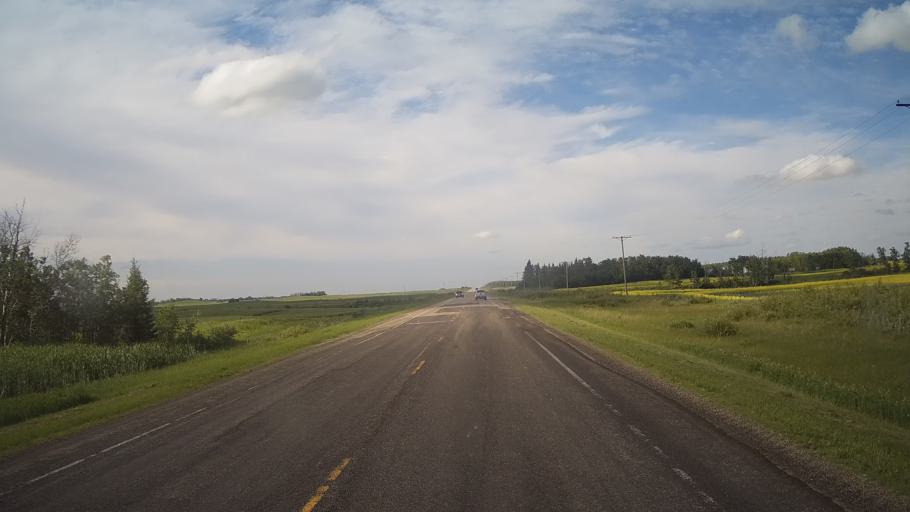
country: CA
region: Saskatchewan
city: Foam Lake
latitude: 51.6023
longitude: -103.8457
